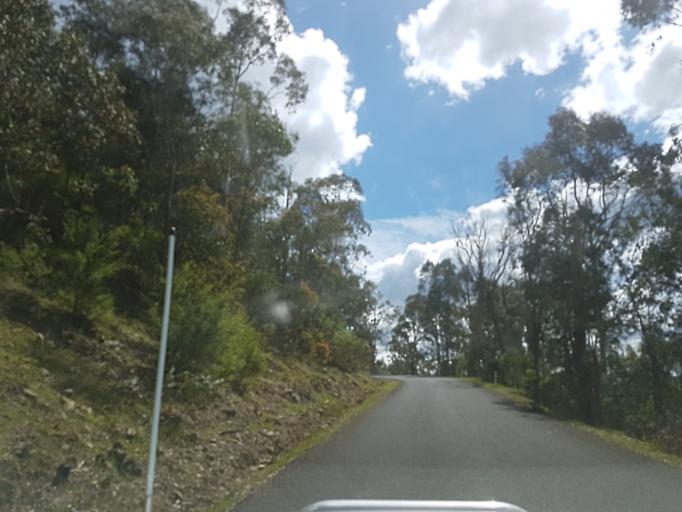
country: AU
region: Victoria
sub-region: East Gippsland
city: Bairnsdale
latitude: -37.4191
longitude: 147.2538
